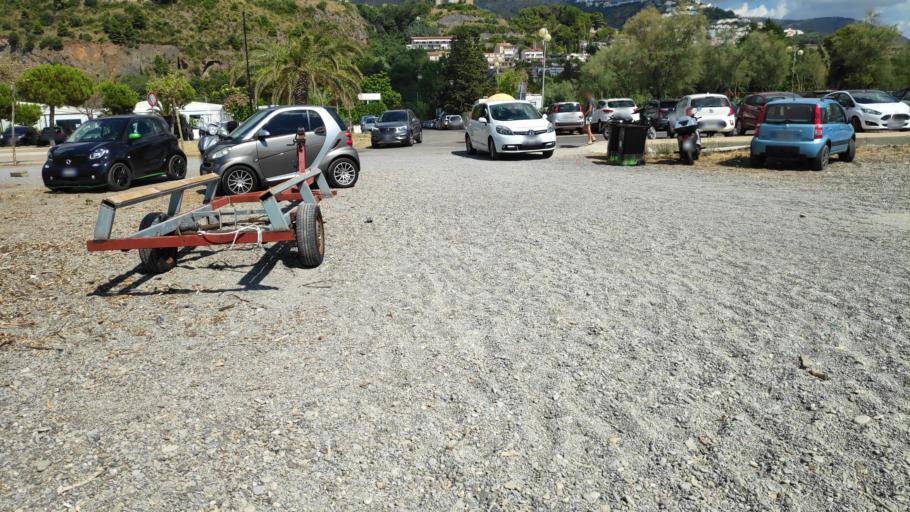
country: IT
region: Calabria
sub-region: Provincia di Cosenza
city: Praia a Mare
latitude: 39.8750
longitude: 15.7844
